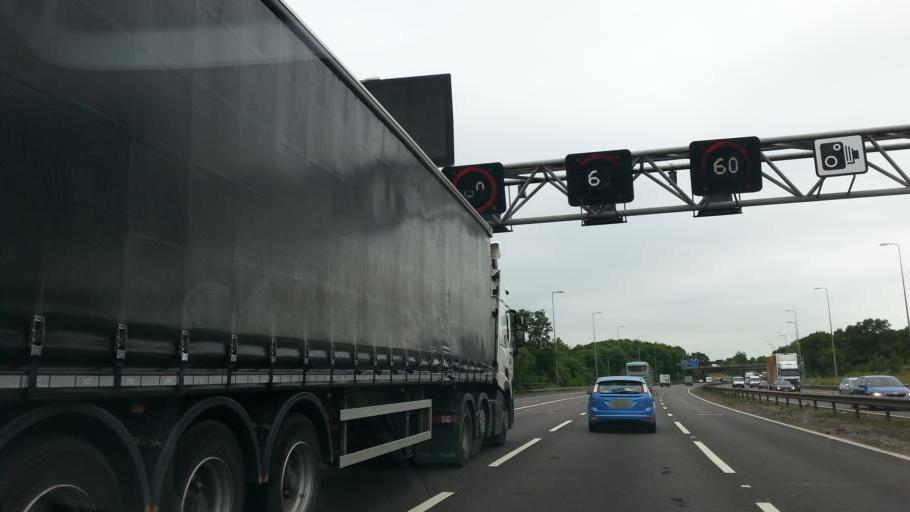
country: GB
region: England
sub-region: Solihull
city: Cheswick Green
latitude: 52.3707
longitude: -1.7925
